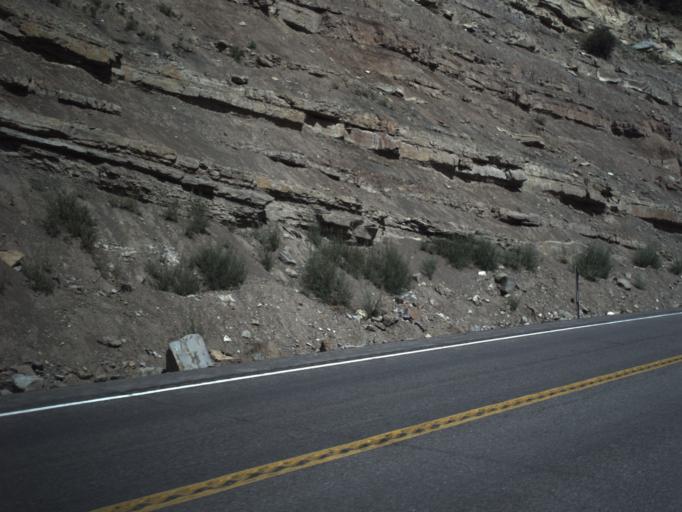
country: US
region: Utah
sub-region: Carbon County
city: Helper
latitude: 39.8078
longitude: -110.9434
